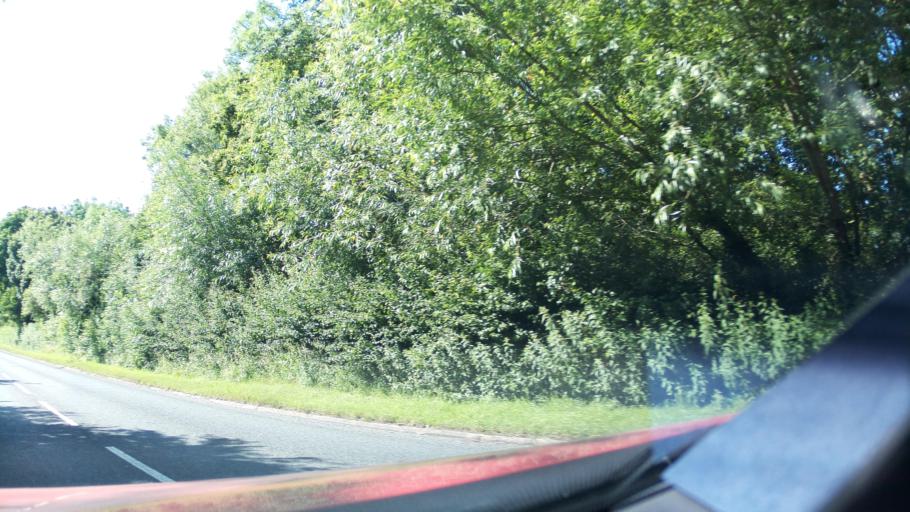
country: GB
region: England
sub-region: Warwickshire
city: Studley
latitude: 52.2993
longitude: -1.8900
